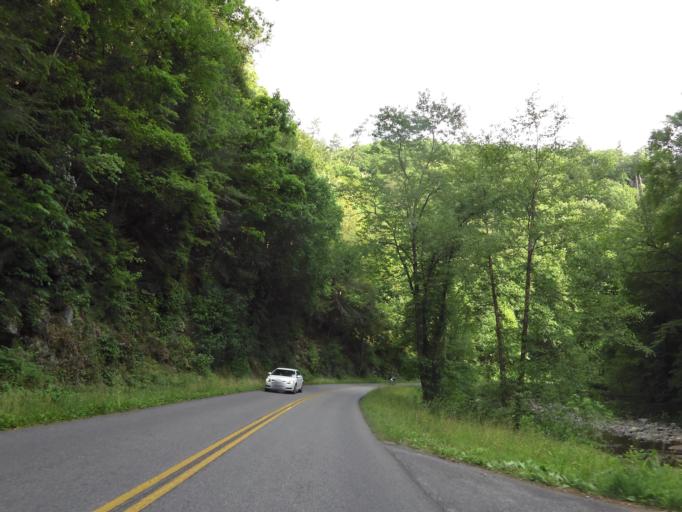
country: US
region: Tennessee
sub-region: Sevier County
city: Pigeon Forge
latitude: 35.6661
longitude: -83.6987
